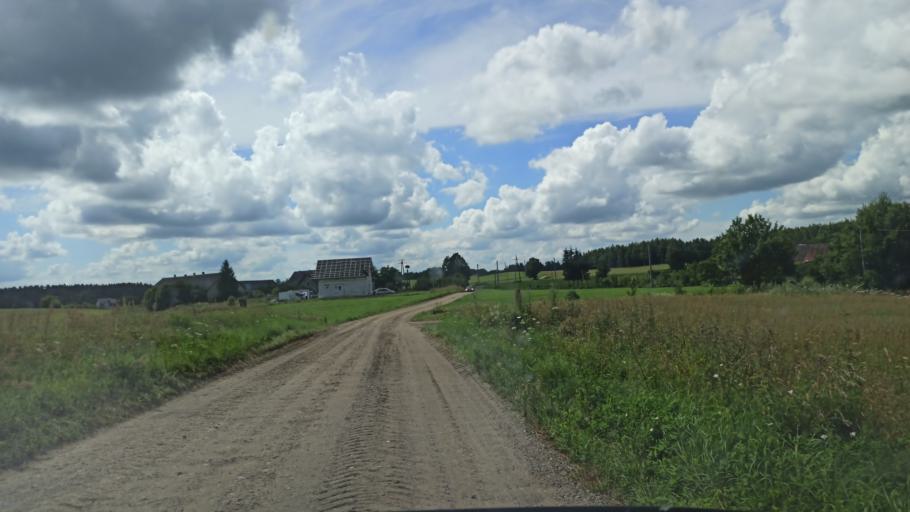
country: PL
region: Warmian-Masurian Voivodeship
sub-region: Powiat ostrodzki
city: Morag
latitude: 53.8650
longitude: 20.0405
